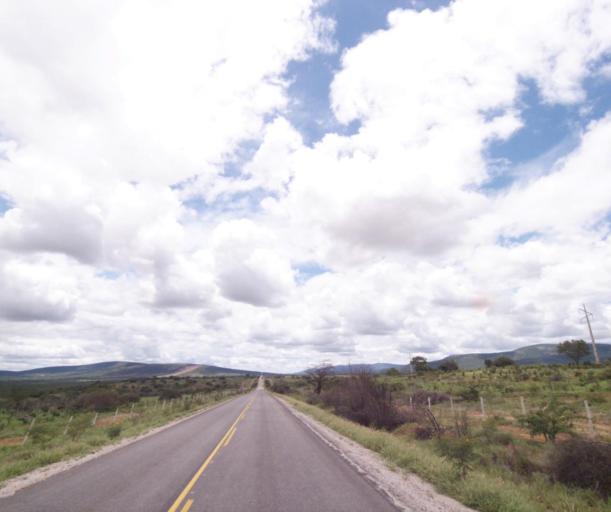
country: BR
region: Bahia
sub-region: Brumado
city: Brumado
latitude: -14.1552
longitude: -41.5169
